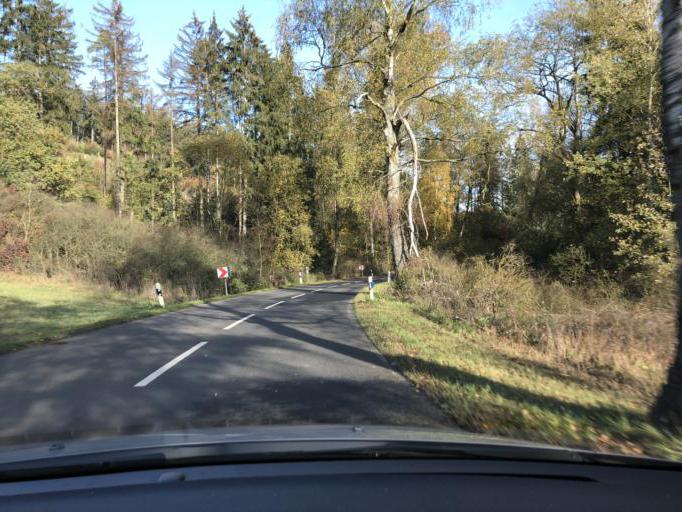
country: DE
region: Thuringia
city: Reurieth
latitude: 50.4266
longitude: 10.6305
